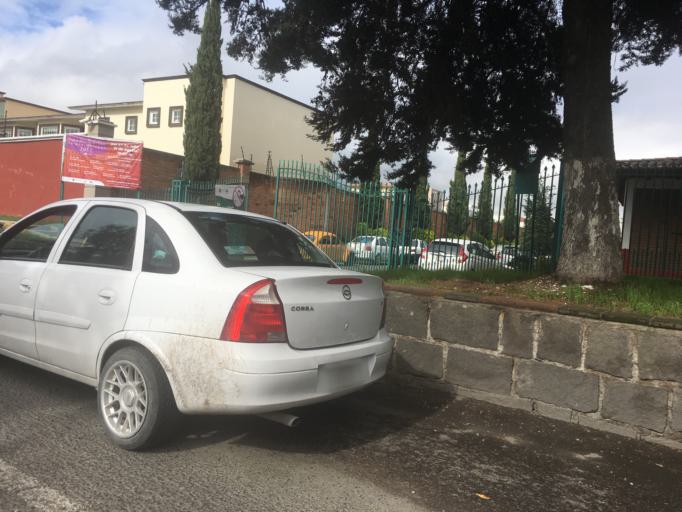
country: MX
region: Morelos
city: Metepec
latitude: 19.2682
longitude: -99.6073
